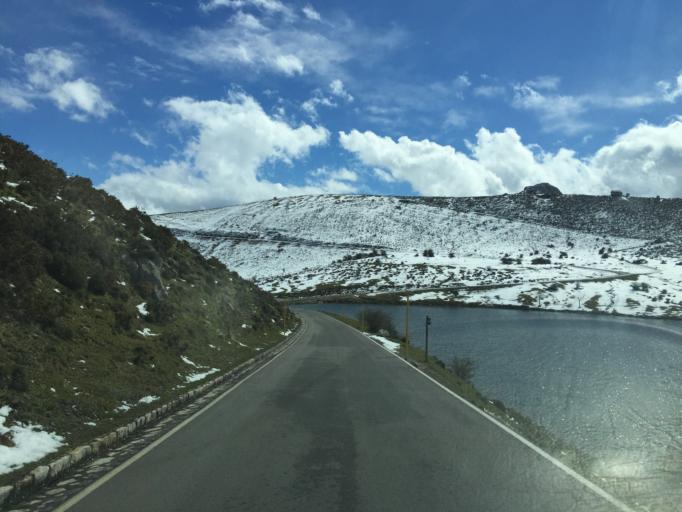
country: ES
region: Asturias
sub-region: Province of Asturias
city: Amieva
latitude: 43.2740
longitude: -4.9913
